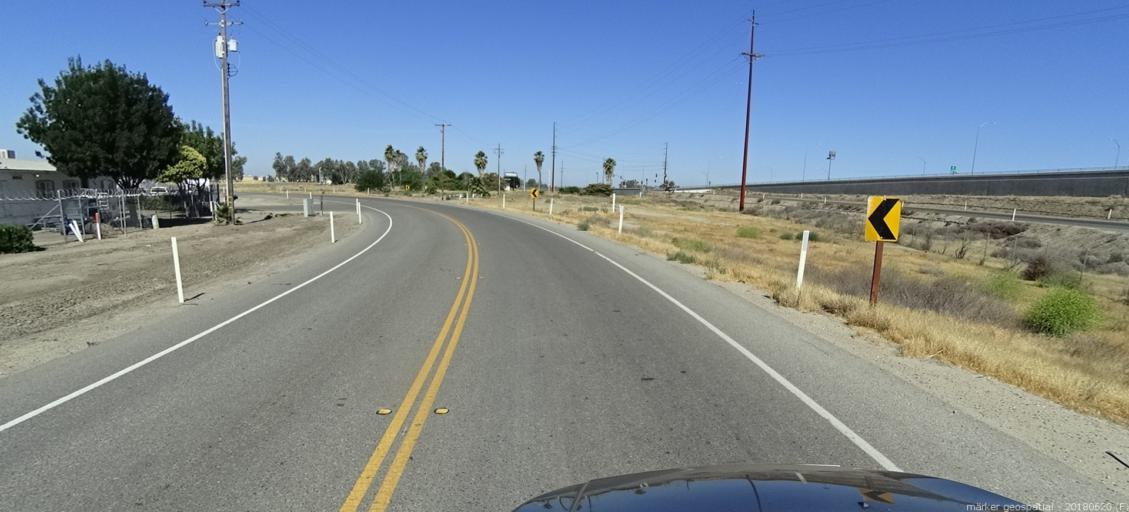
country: US
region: California
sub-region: Madera County
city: Parkwood
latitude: 36.9228
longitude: -120.0221
